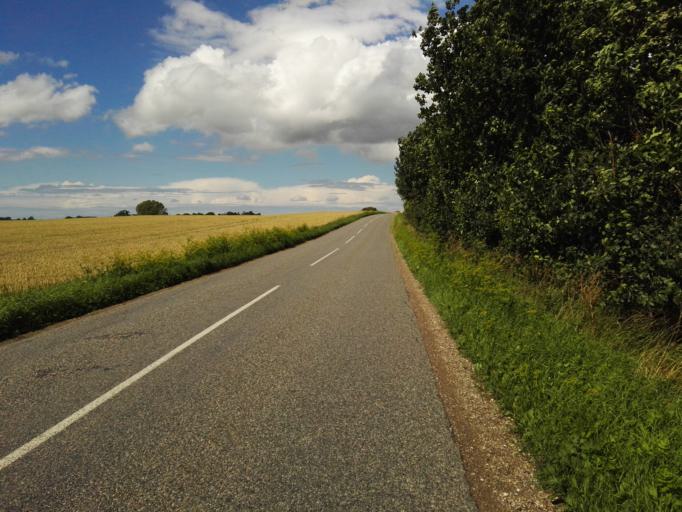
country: DK
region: Capital Region
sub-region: Egedal Kommune
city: Vekso
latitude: 55.7784
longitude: 12.2334
